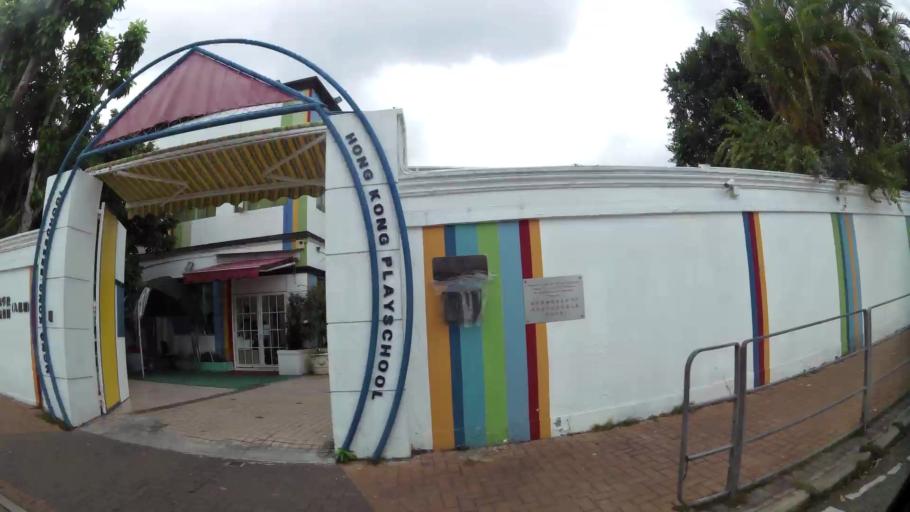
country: HK
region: Kowloon City
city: Kowloon
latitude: 22.3296
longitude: 114.1771
